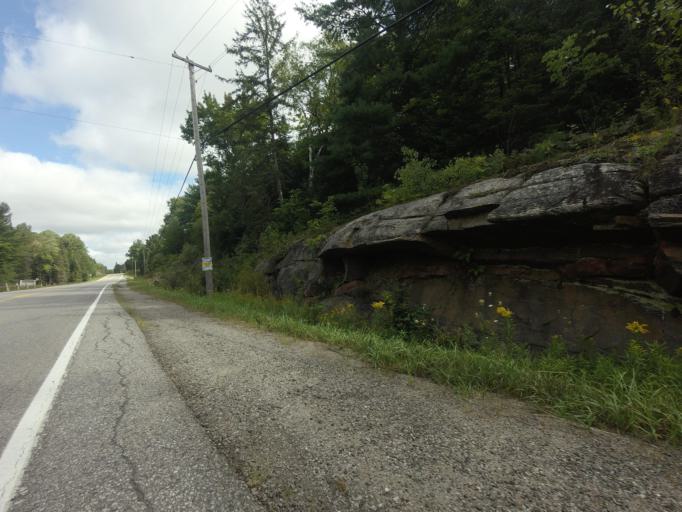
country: CA
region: Ontario
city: Omemee
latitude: 44.7917
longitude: -78.6413
